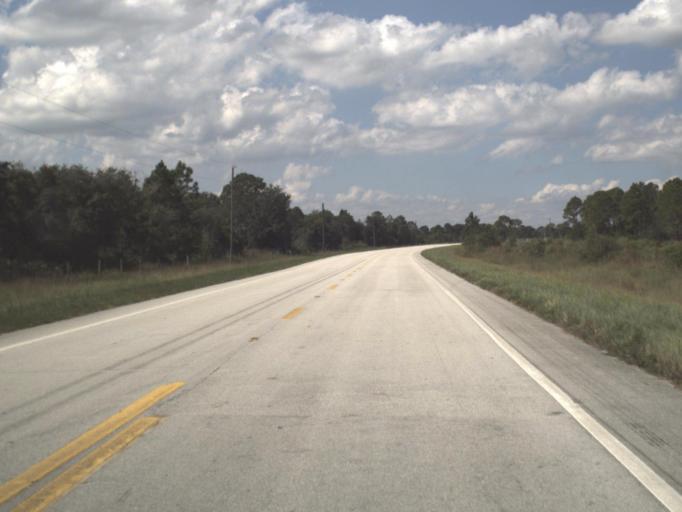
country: US
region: Florida
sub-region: Highlands County
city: Lake Placid
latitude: 27.3816
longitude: -81.1217
